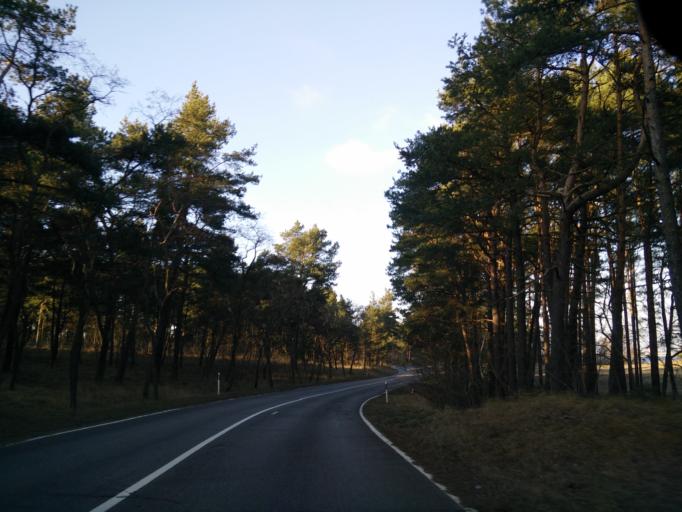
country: LT
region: Klaipedos apskritis
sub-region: Klaipeda
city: Klaipeda
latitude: 55.6348
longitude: 21.1298
